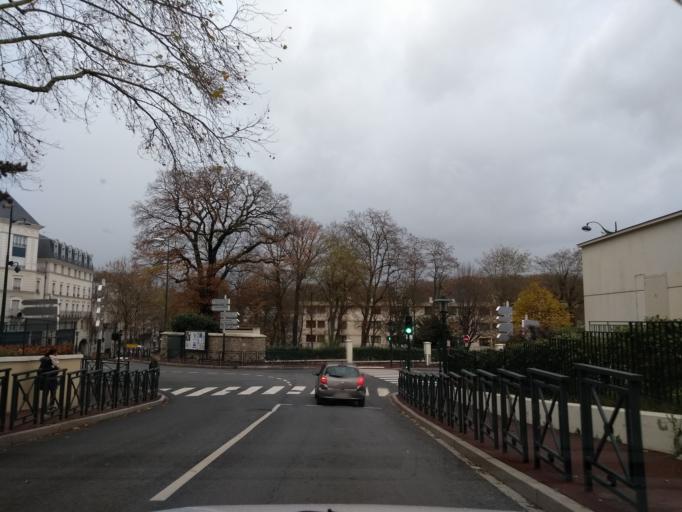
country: FR
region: Ile-de-France
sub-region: Departement des Hauts-de-Seine
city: Le Plessis-Robinson
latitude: 48.7821
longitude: 2.2592
